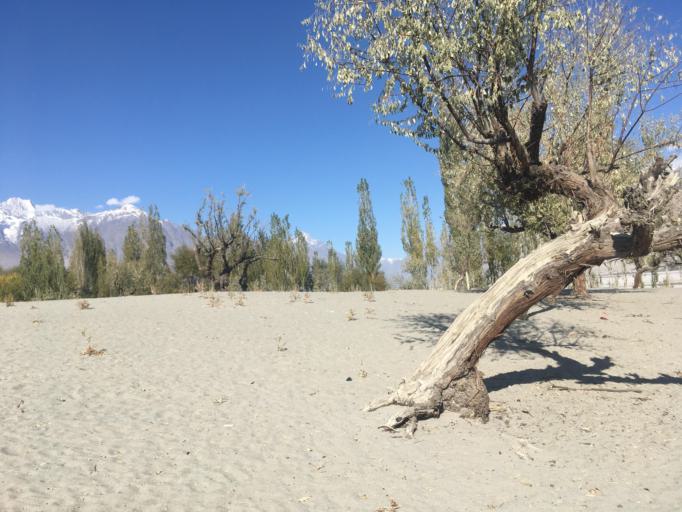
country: PK
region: Gilgit-Baltistan
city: Skardu
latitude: 35.3220
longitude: 75.6057
